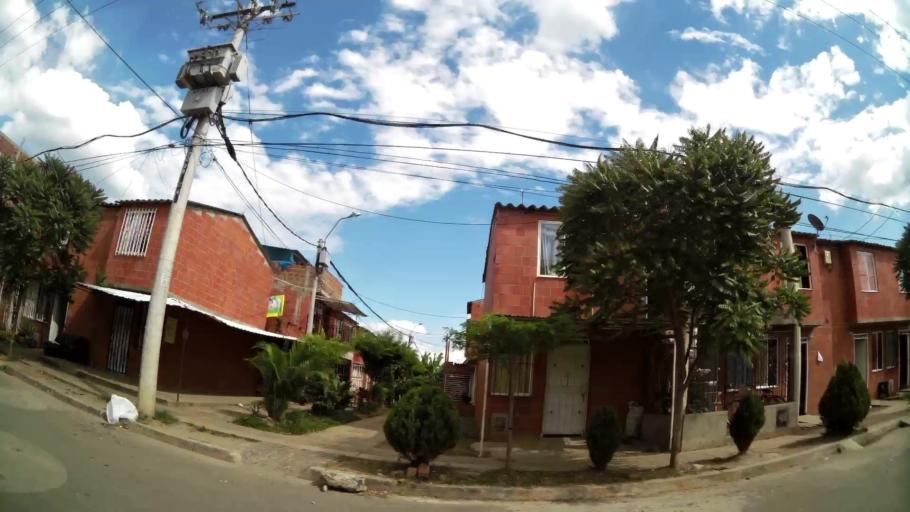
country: CO
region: Valle del Cauca
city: Cali
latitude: 3.3939
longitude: -76.5072
